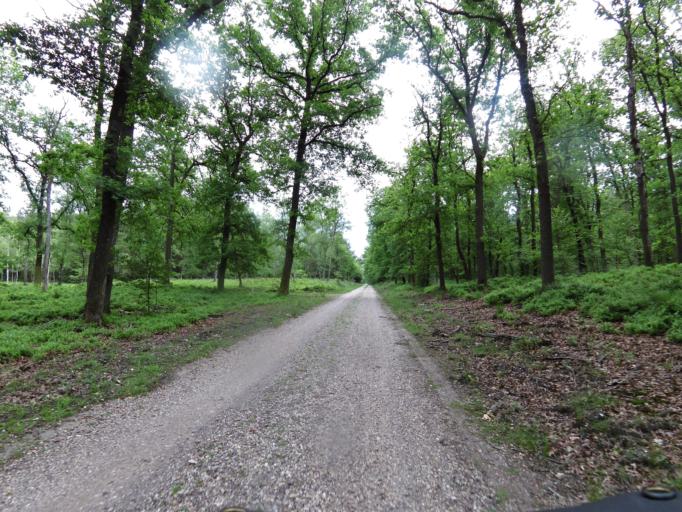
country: NL
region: Gelderland
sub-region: Gemeente Apeldoorn
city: Uddel
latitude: 52.2694
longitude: 5.8217
